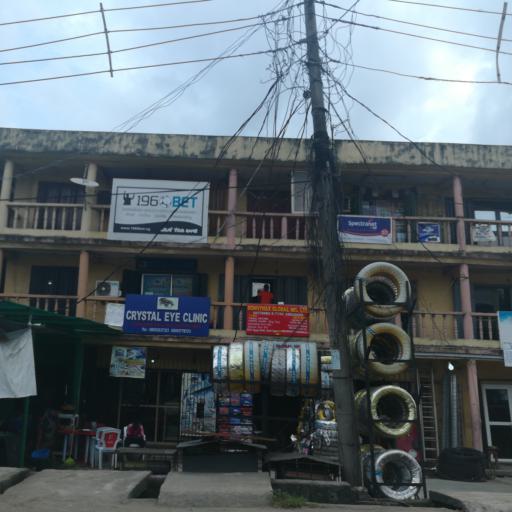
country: NG
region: Lagos
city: Ojota
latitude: 6.5863
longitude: 3.3838
